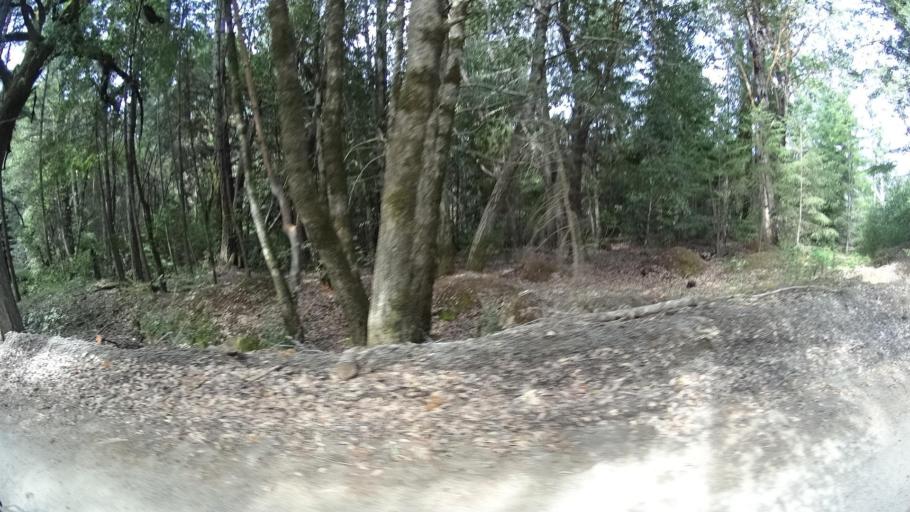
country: US
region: California
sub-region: Humboldt County
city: Redway
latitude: 40.0295
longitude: -123.8412
